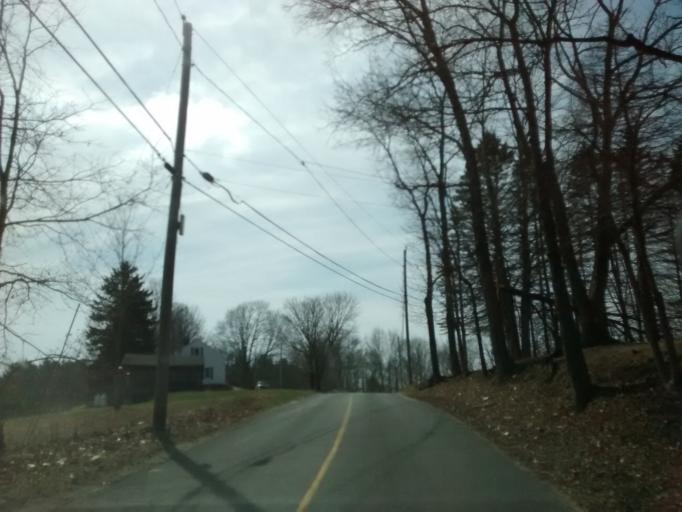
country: US
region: Massachusetts
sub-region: Worcester County
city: Charlton
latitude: 42.1256
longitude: -72.0073
